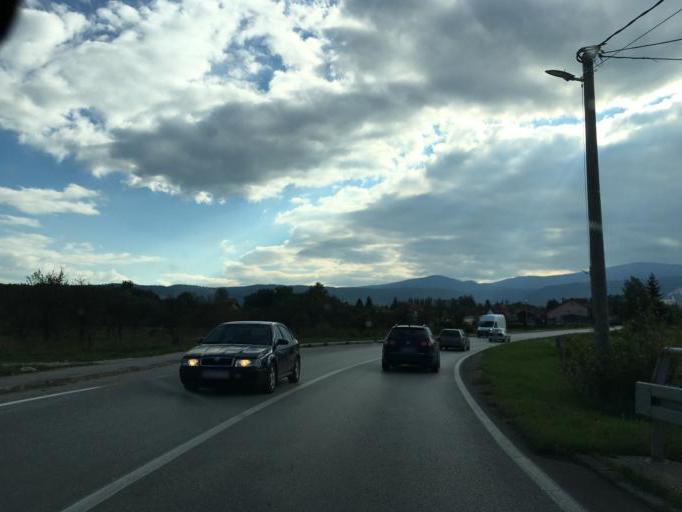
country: BA
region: Federation of Bosnia and Herzegovina
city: Bugojno
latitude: 44.0606
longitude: 17.4656
